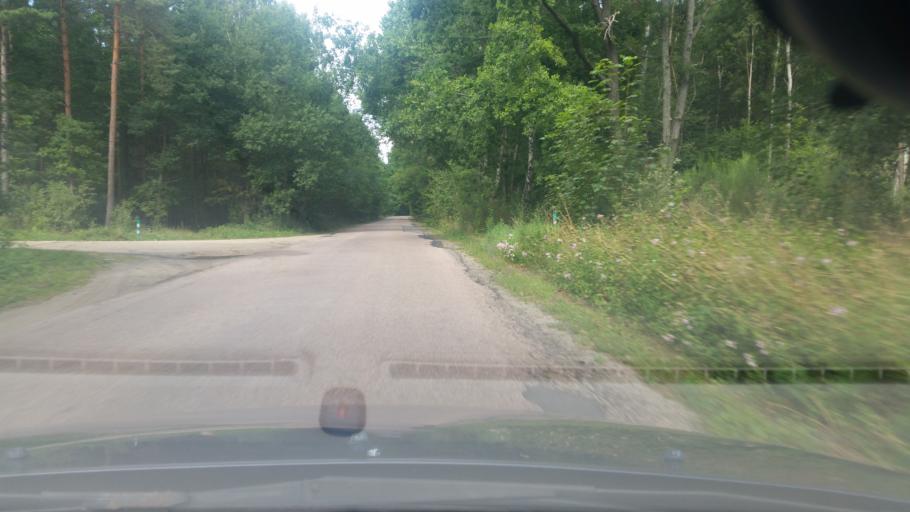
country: PL
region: Pomeranian Voivodeship
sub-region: Powiat wejherowski
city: Choczewo
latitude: 54.7595
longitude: 17.7740
